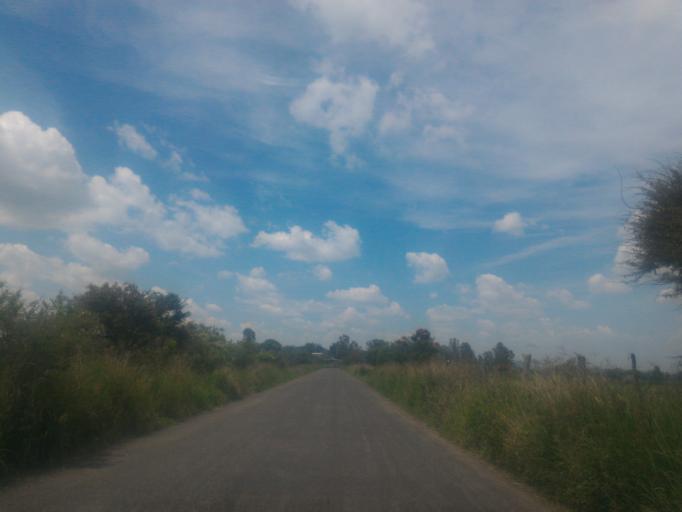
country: MX
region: Guanajuato
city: Ciudad Manuel Doblado
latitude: 20.8175
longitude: -102.0630
